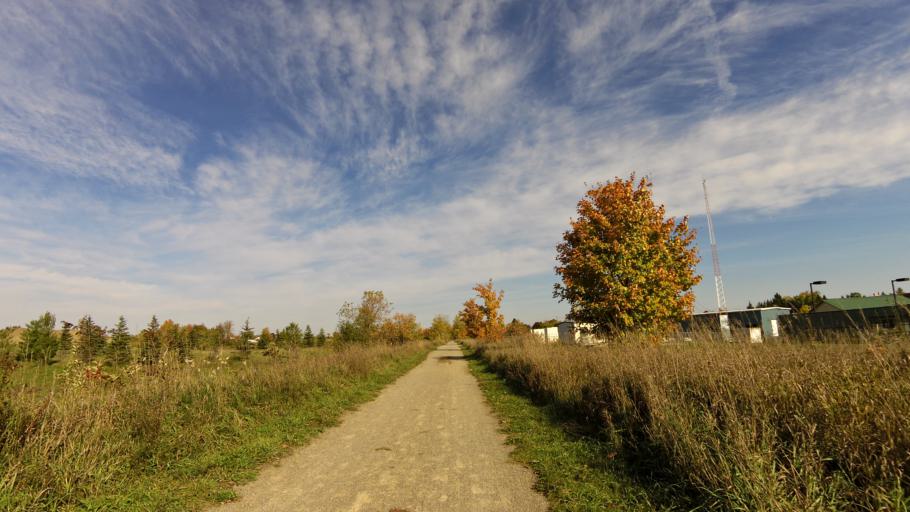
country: CA
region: Ontario
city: Orangeville
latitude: 43.7797
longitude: -80.0698
